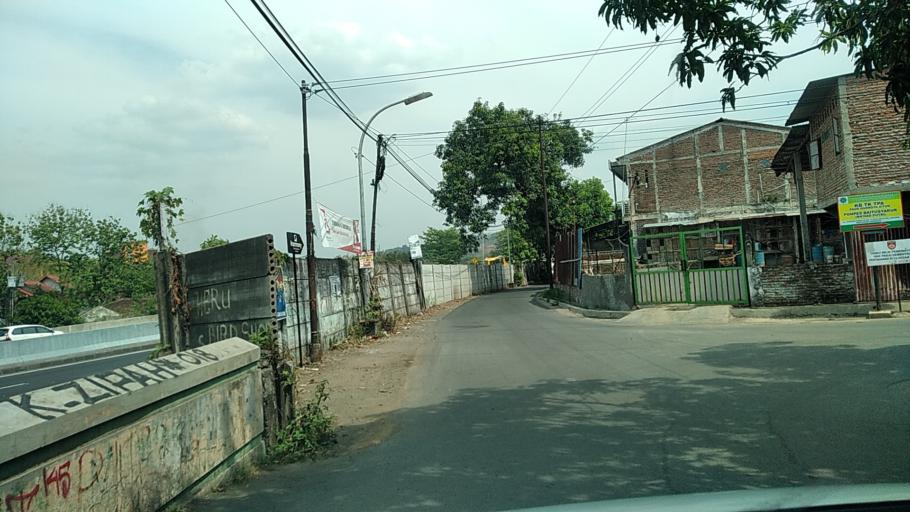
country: ID
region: Central Java
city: Semarang
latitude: -7.0334
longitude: 110.4314
